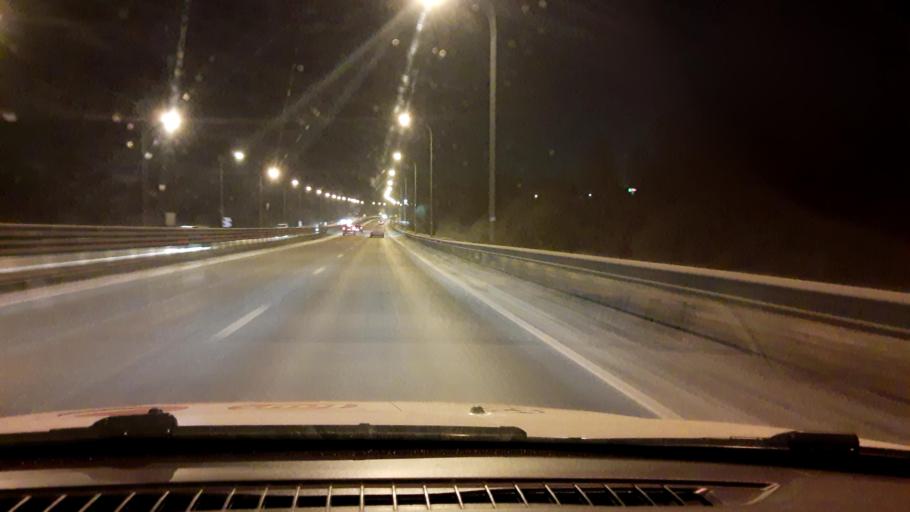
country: RU
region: Nizjnij Novgorod
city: Afonino
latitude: 56.2328
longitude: 44.0560
